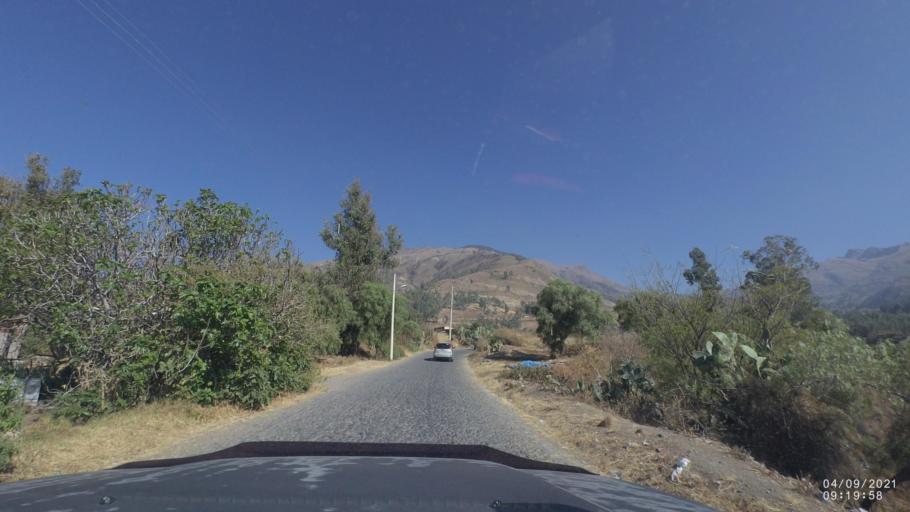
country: BO
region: Cochabamba
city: Sipe Sipe
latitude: -17.3654
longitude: -66.3605
